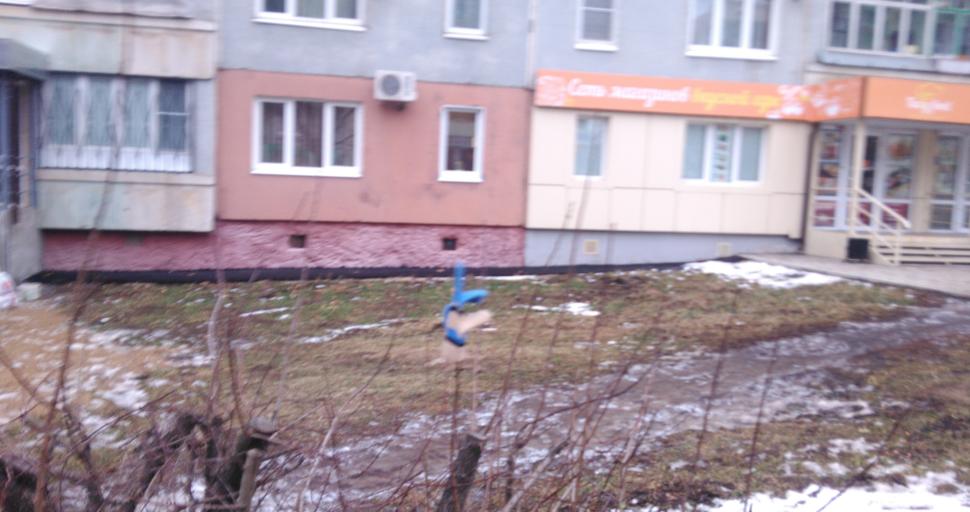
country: RU
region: Tula
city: Tula
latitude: 54.2014
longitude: 37.6404
